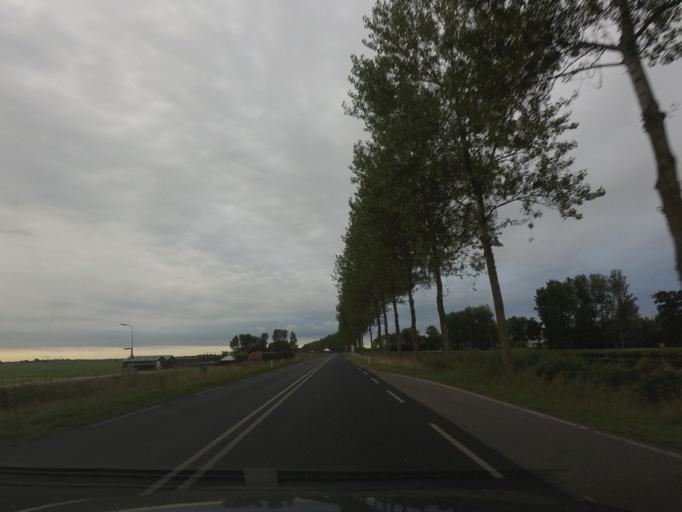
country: NL
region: North Holland
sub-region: Gemeente Alkmaar
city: Alkmaar
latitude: 52.5847
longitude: 4.7533
